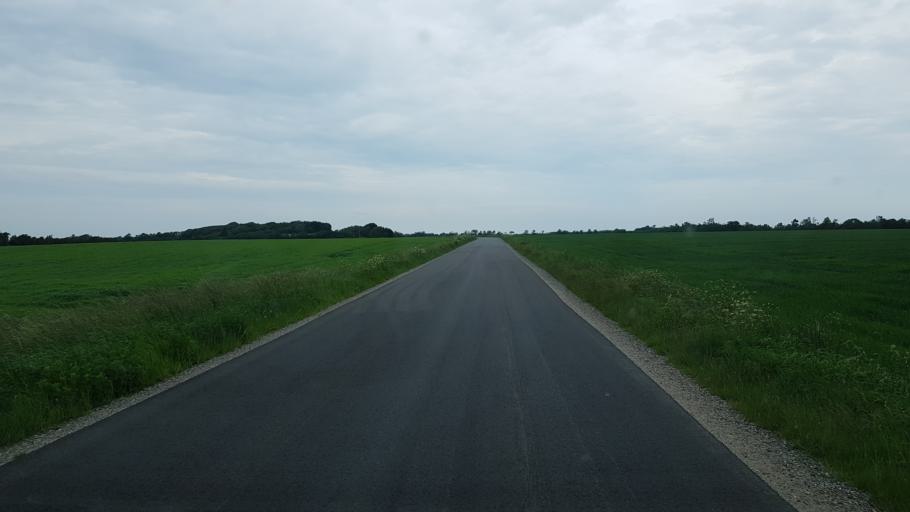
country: DK
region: South Denmark
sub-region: Varde Kommune
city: Oksbol
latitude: 55.7375
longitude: 8.3727
